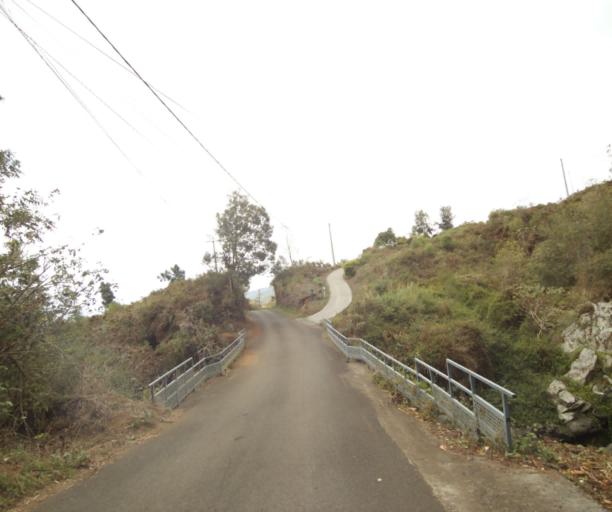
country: RE
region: Reunion
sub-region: Reunion
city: Saint-Paul
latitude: -21.0131
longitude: 55.3364
